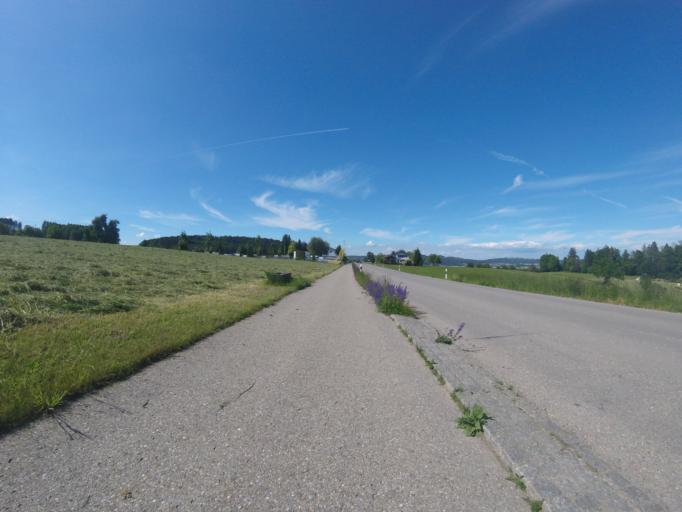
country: CH
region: Saint Gallen
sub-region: Wahlkreis Toggenburg
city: Kirchberg
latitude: 47.4223
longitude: 9.0623
